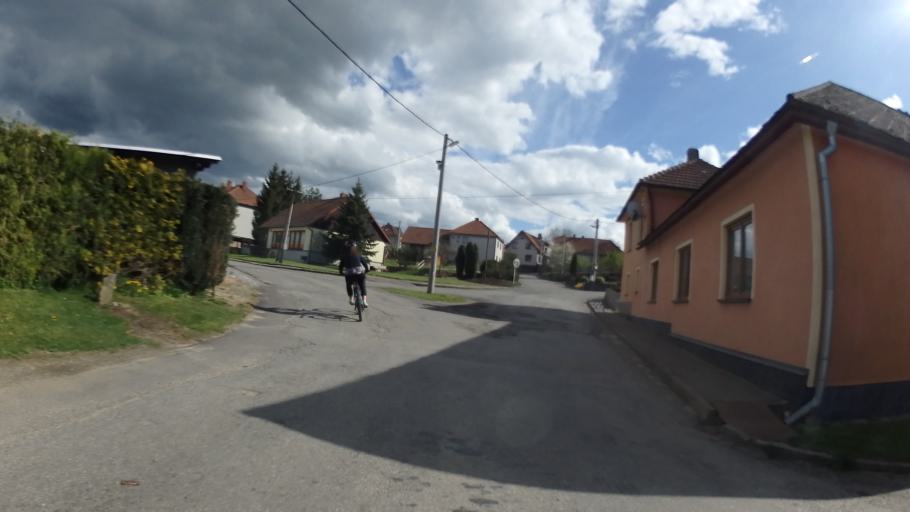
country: CZ
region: Vysocina
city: Merin
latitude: 49.3469
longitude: 15.8787
